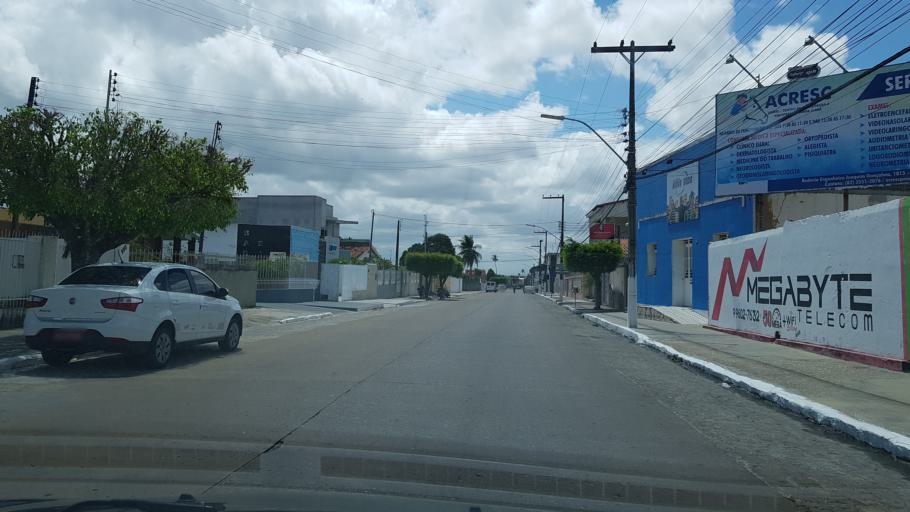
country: BR
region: Alagoas
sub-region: Penedo
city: Penedo
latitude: -10.2818
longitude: -36.5640
